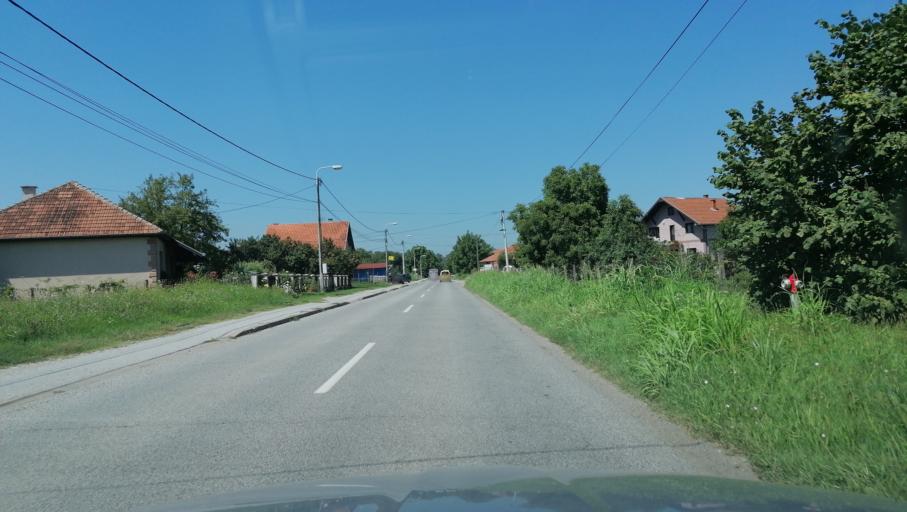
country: RS
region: Central Serbia
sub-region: Raski Okrug
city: Kraljevo
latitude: 43.6900
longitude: 20.6021
